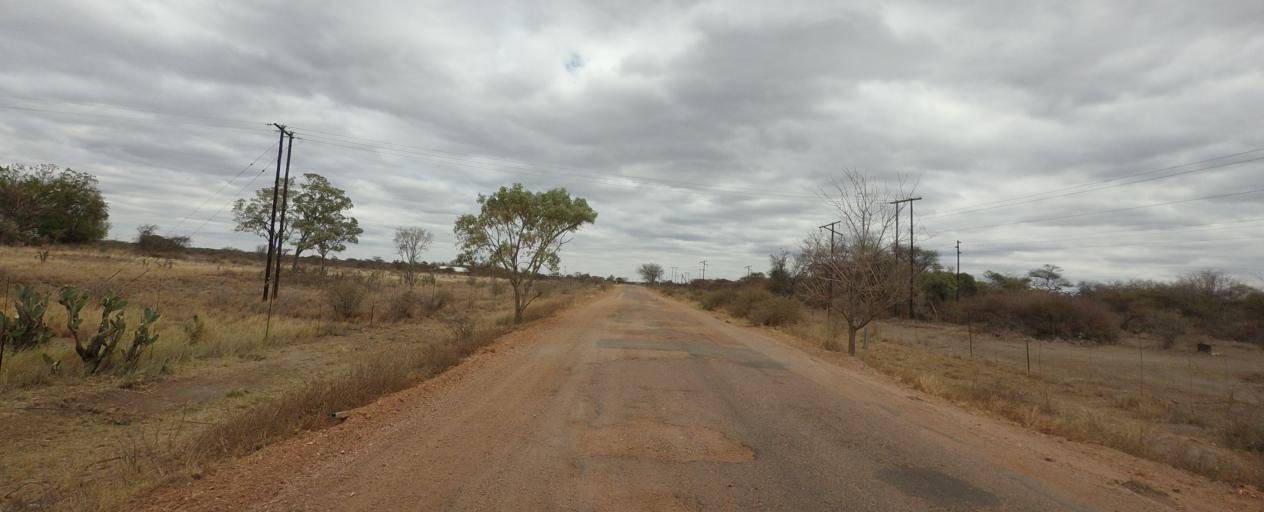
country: BW
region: Central
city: Mathathane
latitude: -22.7428
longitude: 28.4521
